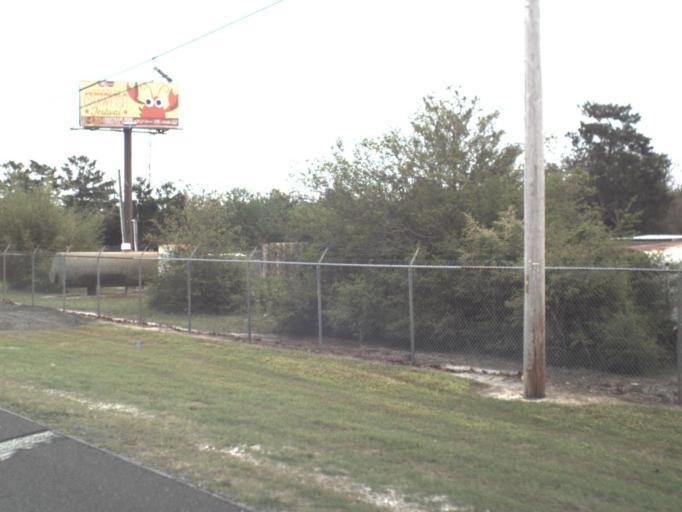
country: US
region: Florida
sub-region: Santa Rosa County
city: Woodlawn Beach
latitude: 30.4023
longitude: -86.9820
